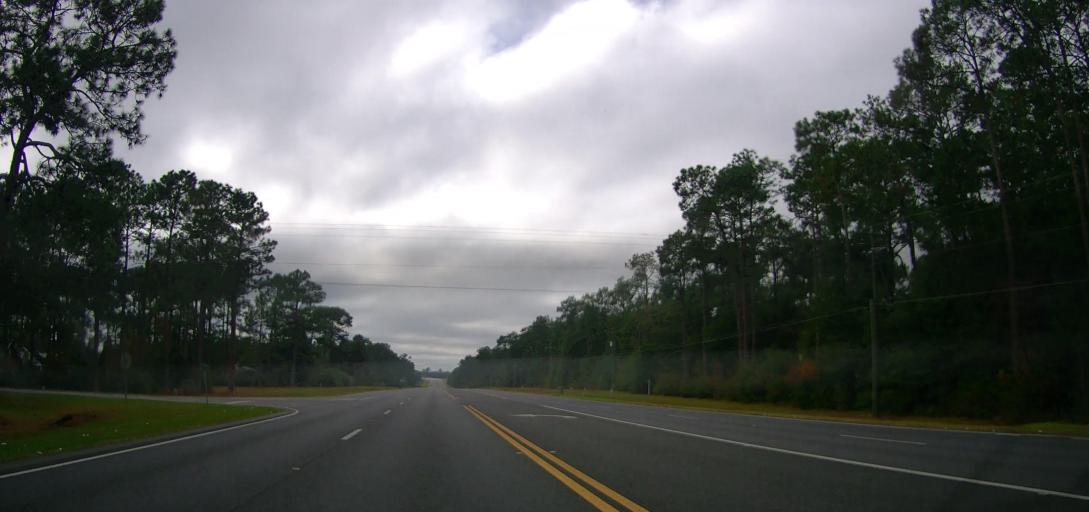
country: US
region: Georgia
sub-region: Colquitt County
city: Moultrie
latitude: 31.0884
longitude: -83.8099
